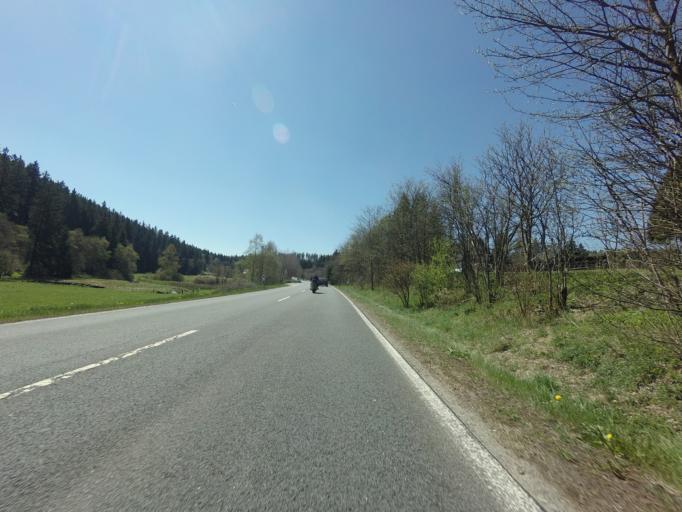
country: DE
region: North Rhine-Westphalia
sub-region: Regierungsbezirk Arnsberg
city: Erndtebruck
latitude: 50.9734
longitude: 8.2048
